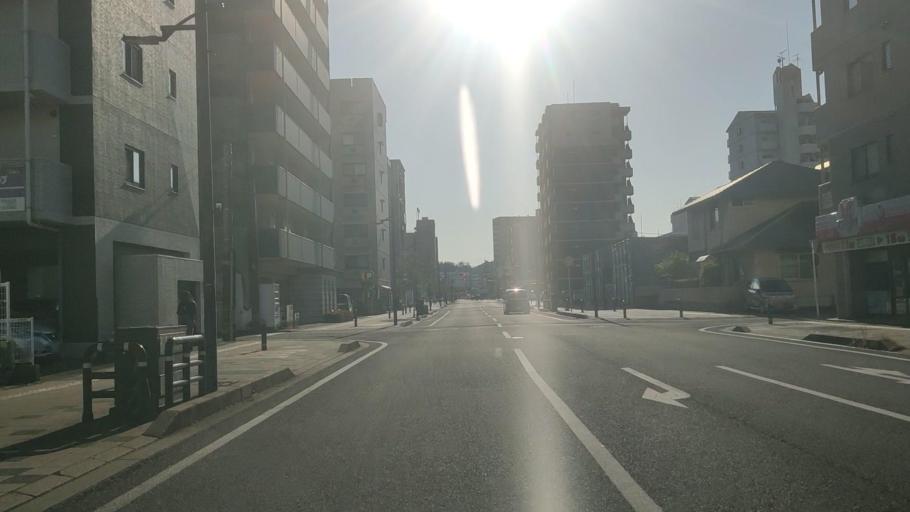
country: JP
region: Oita
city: Oita
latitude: 33.2326
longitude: 131.6032
